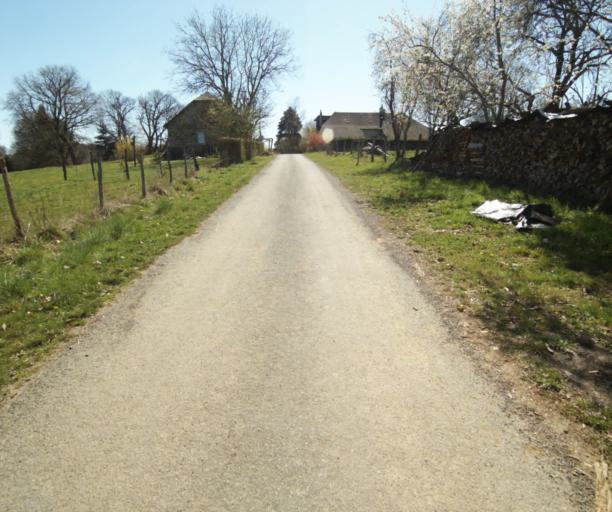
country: FR
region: Limousin
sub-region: Departement de la Correze
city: Uzerche
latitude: 45.4017
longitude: 1.6278
